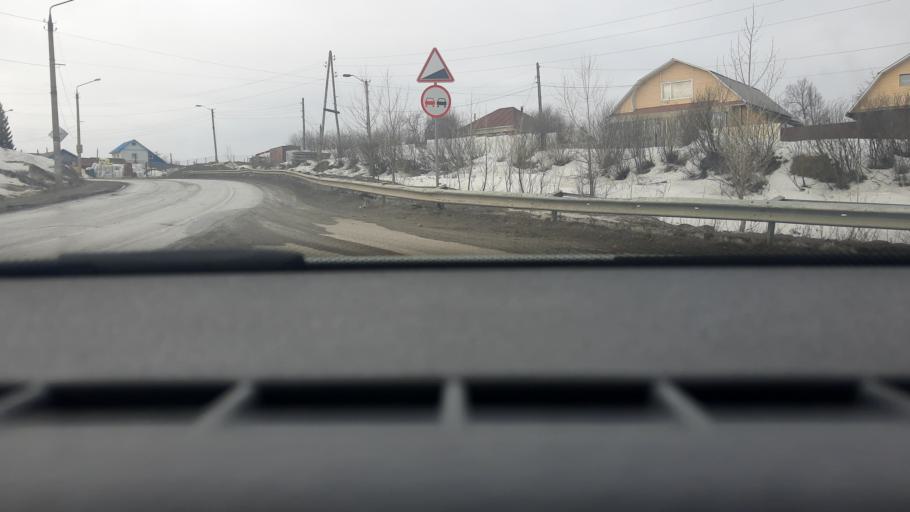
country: RU
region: Chelyabinsk
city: Asha
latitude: 54.9935
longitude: 57.2576
